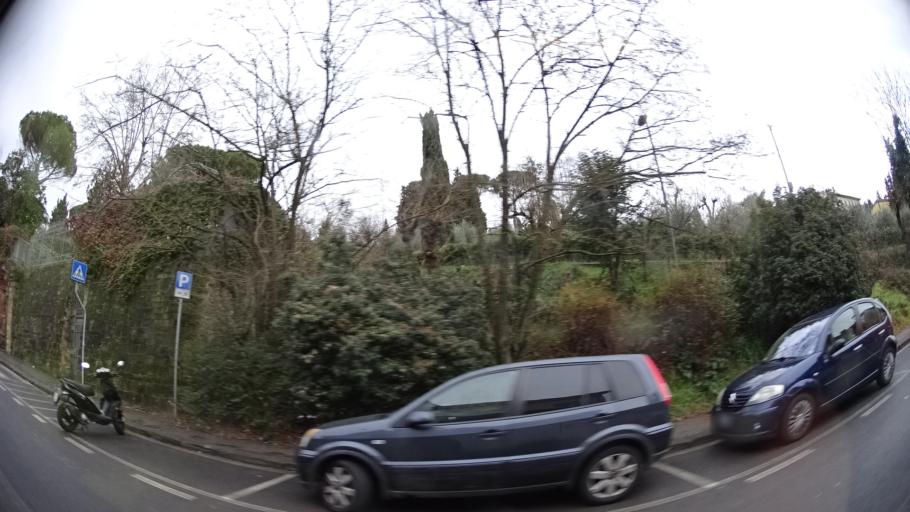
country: IT
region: Tuscany
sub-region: Province of Florence
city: Fiesole
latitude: 43.7941
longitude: 11.2840
